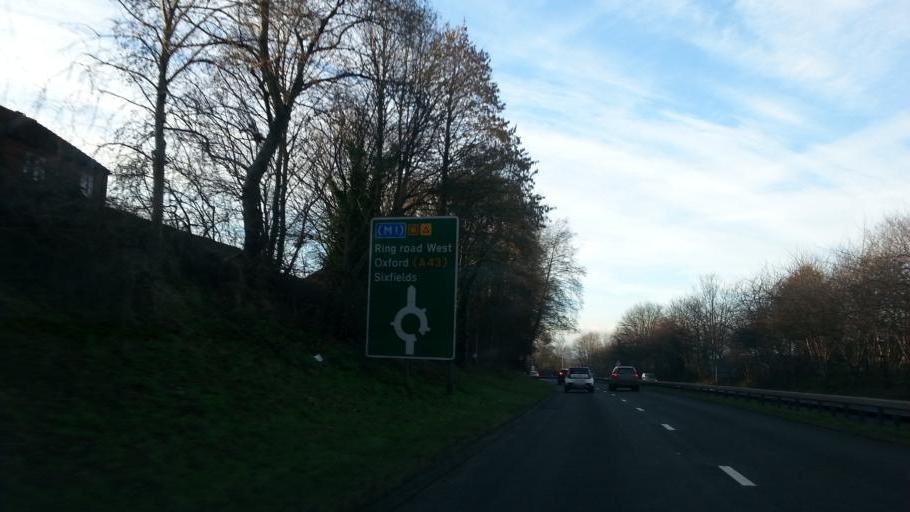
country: GB
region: England
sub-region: Northamptonshire
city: Hardingstone
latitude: 52.2235
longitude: -0.9219
